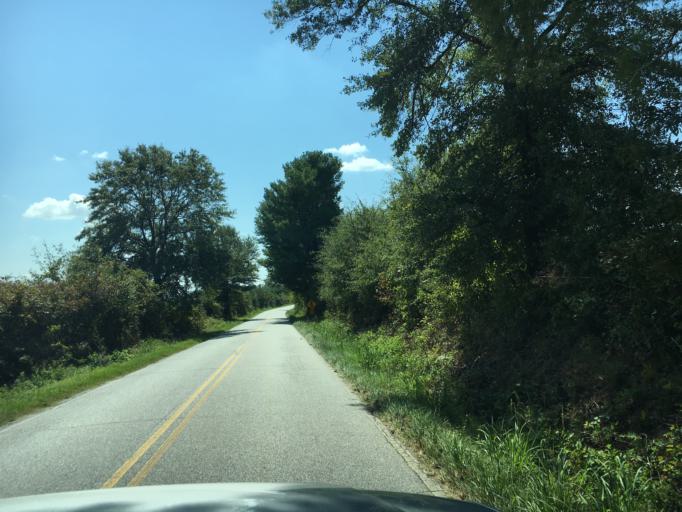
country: US
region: South Carolina
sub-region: Spartanburg County
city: Valley Falls
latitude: 35.0236
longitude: -81.9257
